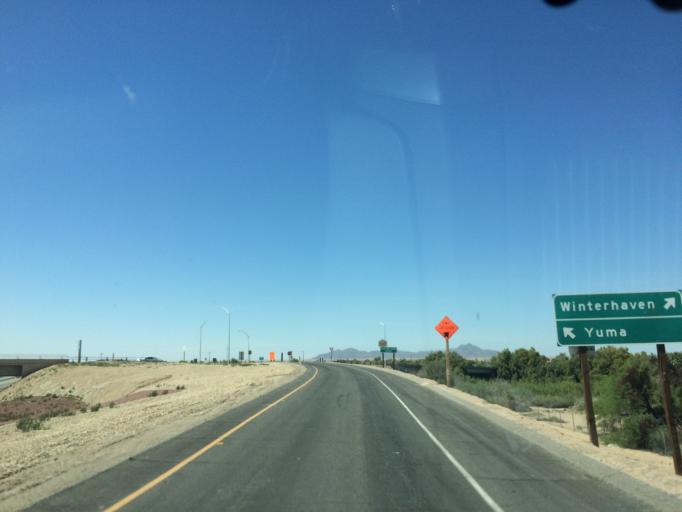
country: US
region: Arizona
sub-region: Yuma County
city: Yuma
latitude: 32.7318
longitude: -114.6233
